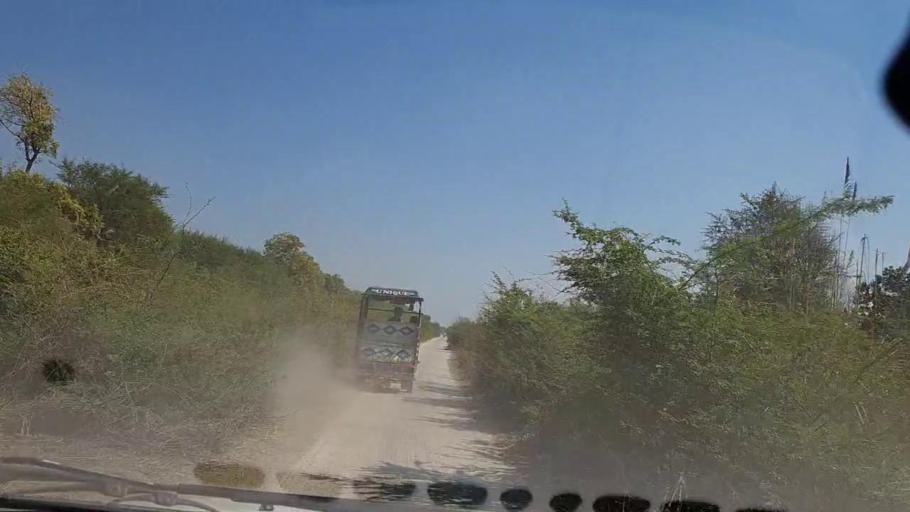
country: PK
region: Sindh
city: Mirpur Khas
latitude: 25.4710
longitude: 69.0383
